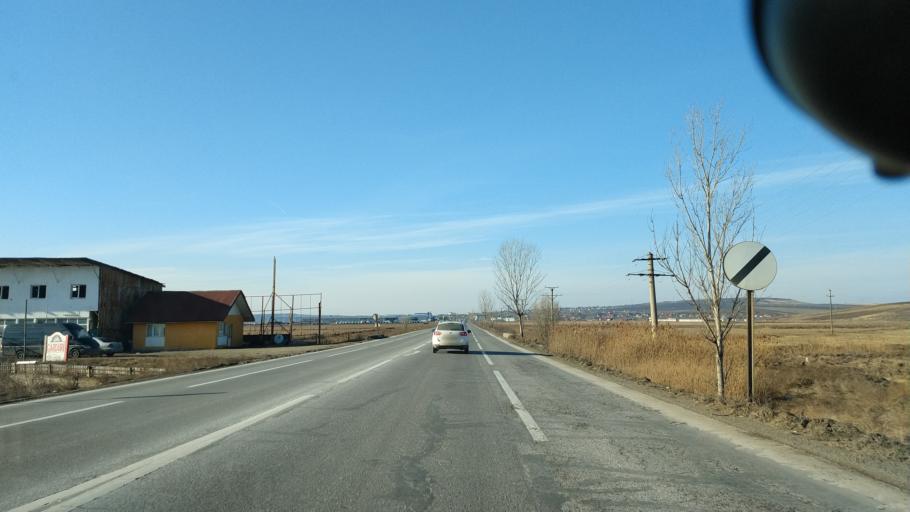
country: RO
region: Iasi
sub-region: Comuna Letcani
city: Letcani
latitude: 47.1865
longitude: 27.4465
